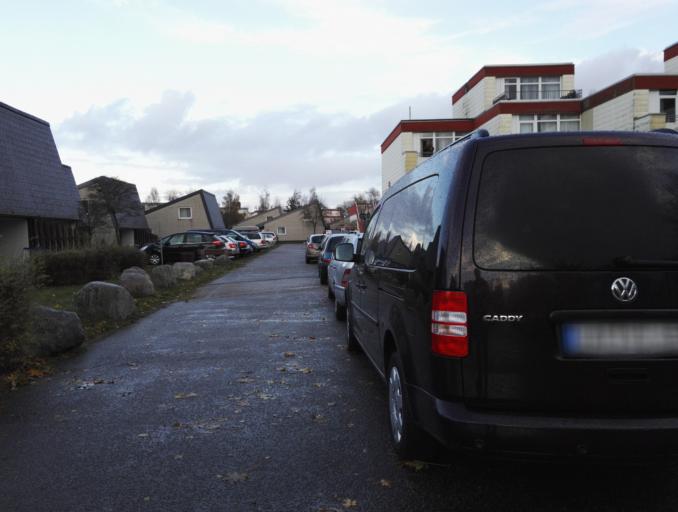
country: DE
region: Schleswig-Holstein
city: Wangels
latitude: 54.3086
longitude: 10.7935
